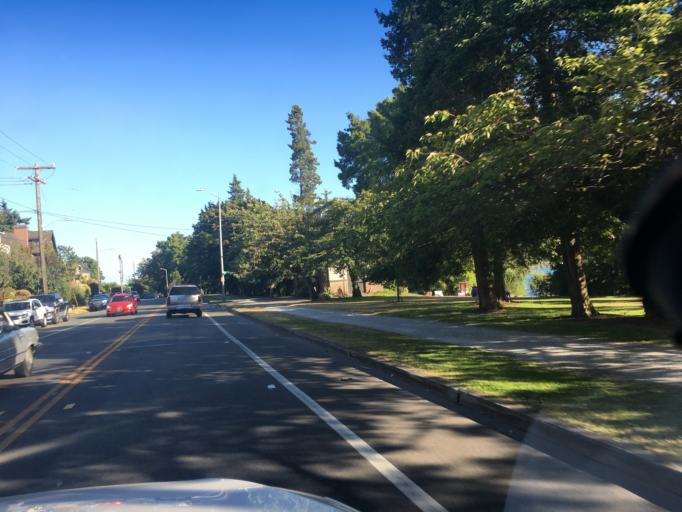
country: US
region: Washington
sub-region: King County
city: Shoreline
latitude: 47.6848
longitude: -122.3355
